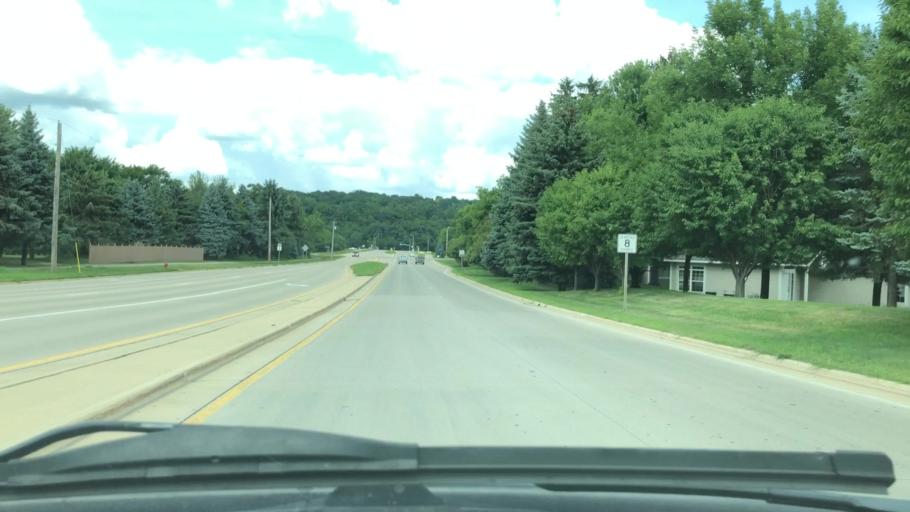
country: US
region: Minnesota
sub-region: Olmsted County
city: Rochester
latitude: 43.9930
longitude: -92.4987
